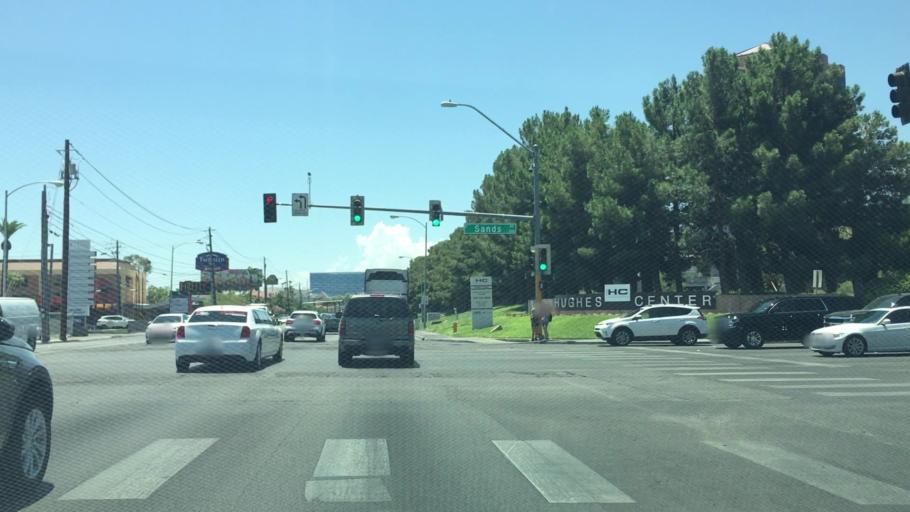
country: US
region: Nevada
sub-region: Clark County
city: Paradise
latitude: 36.1214
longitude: -115.1551
